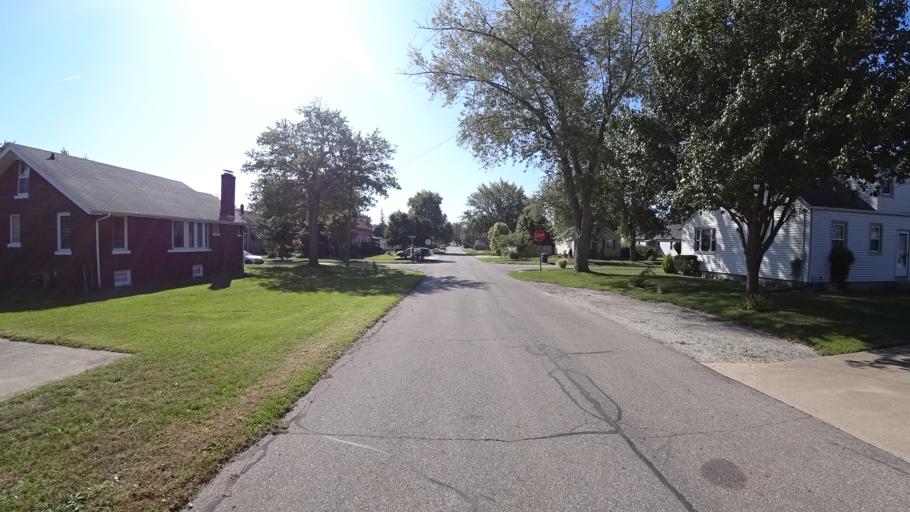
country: US
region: Indiana
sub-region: LaPorte County
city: Michigan City
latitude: 41.7079
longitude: -86.8878
